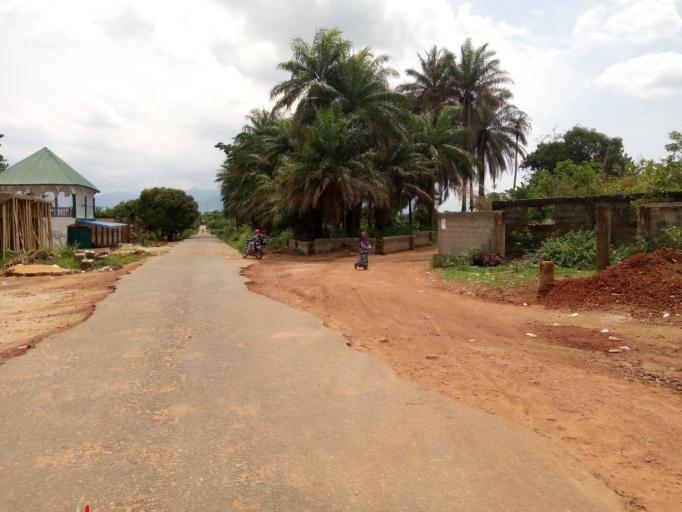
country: SL
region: Western Area
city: Waterloo
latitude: 8.3345
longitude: -13.0241
